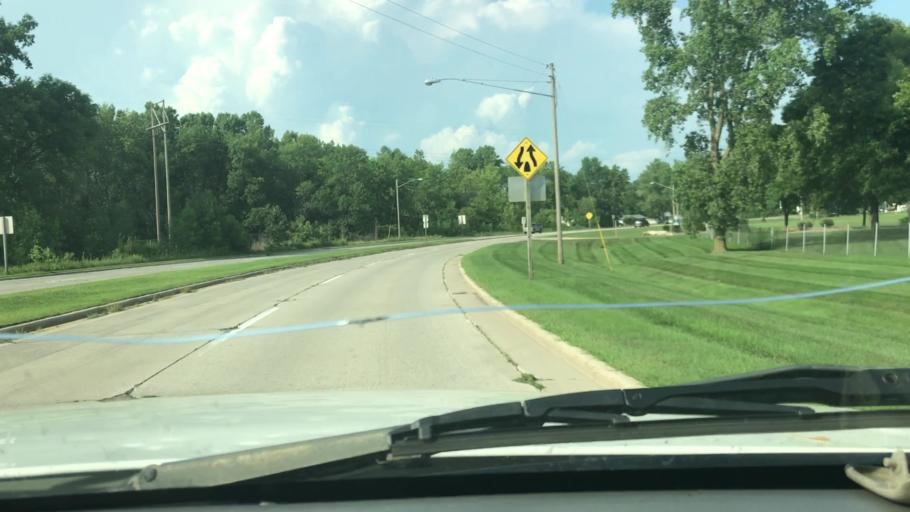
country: US
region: Wisconsin
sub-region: Brown County
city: Green Bay
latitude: 44.5271
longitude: -87.9405
